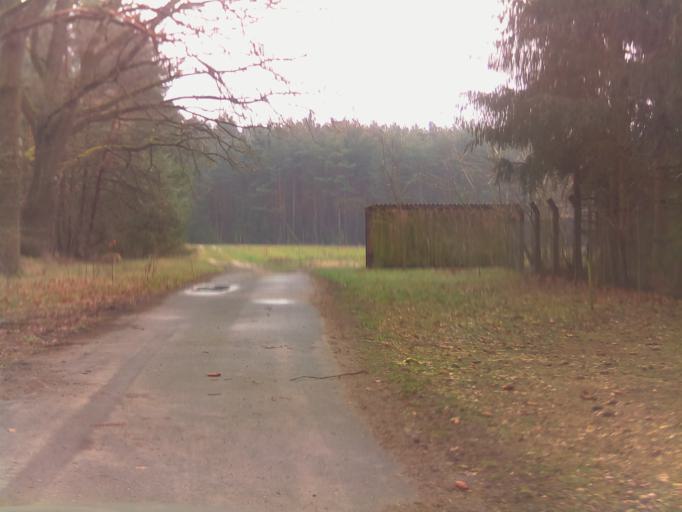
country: DE
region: Brandenburg
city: Schlepzig
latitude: 52.0202
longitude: 13.9848
